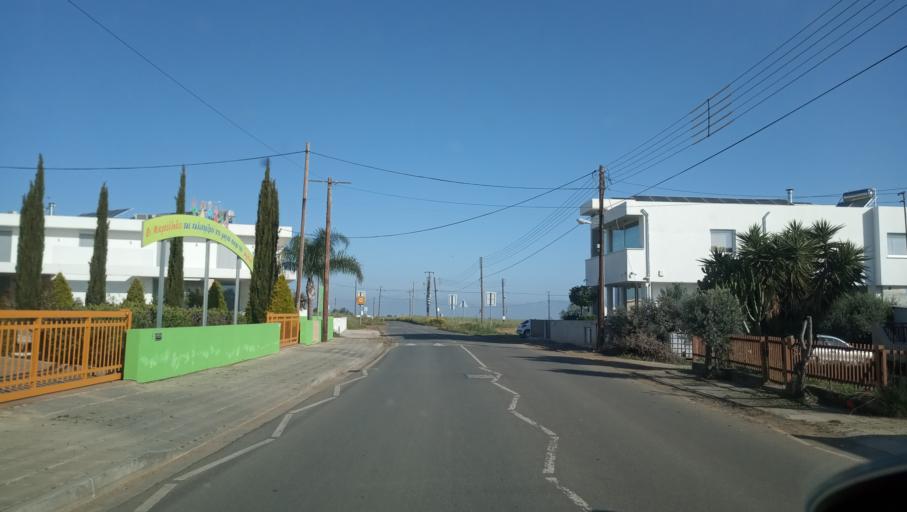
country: CY
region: Lefkosia
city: Tseri
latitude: 35.0792
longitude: 33.3187
